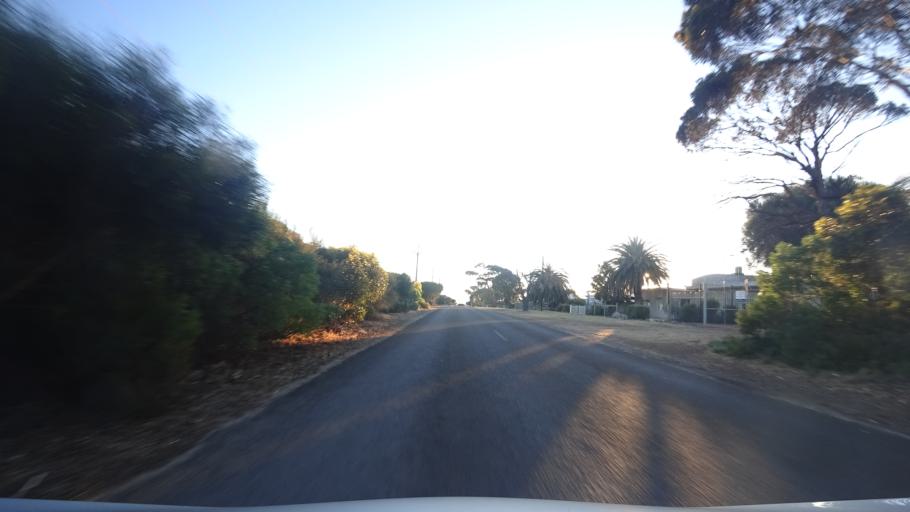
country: AU
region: South Australia
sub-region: Kangaroo Island
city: Kingscote
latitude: -35.6458
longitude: 137.6308
